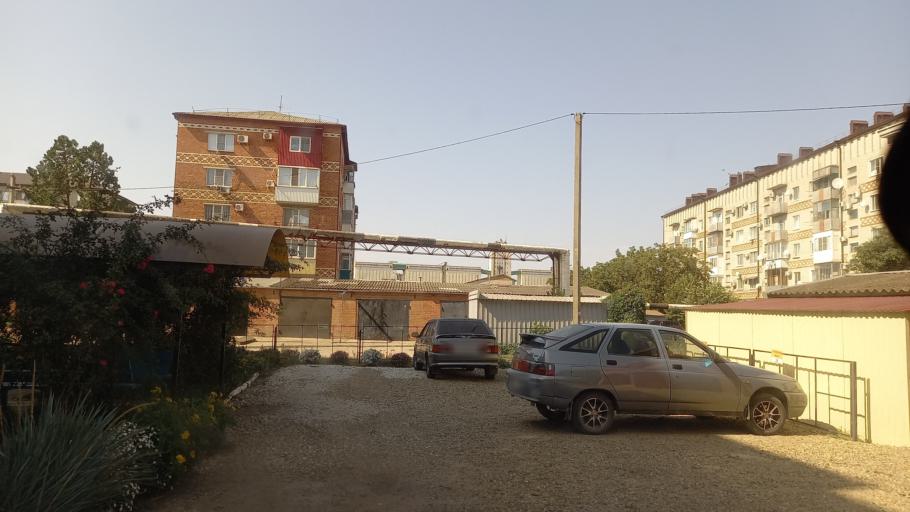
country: RU
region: Krasnodarskiy
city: Bryukhovetskaya
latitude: 45.8018
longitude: 38.9990
